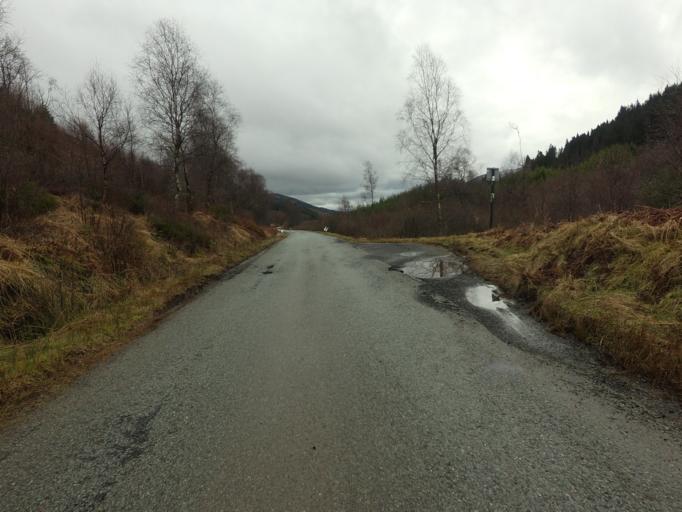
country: GB
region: Scotland
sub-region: West Dunbartonshire
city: Balloch
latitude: 56.2415
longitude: -4.5702
